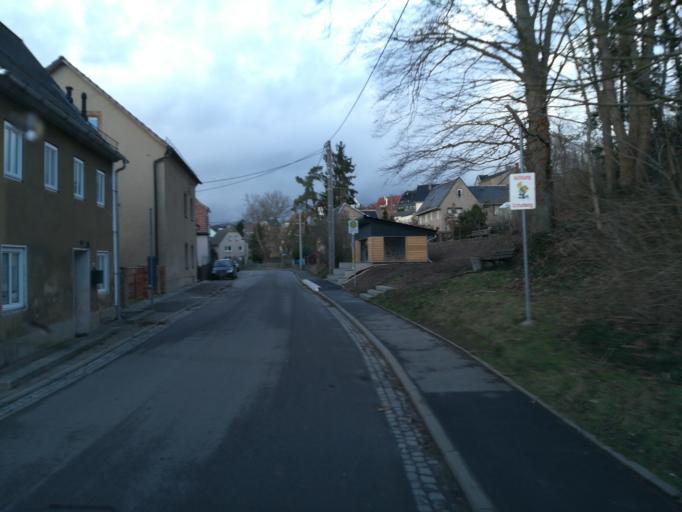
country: DE
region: Saxony
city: Wechselburg
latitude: 51.0017
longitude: 12.7777
